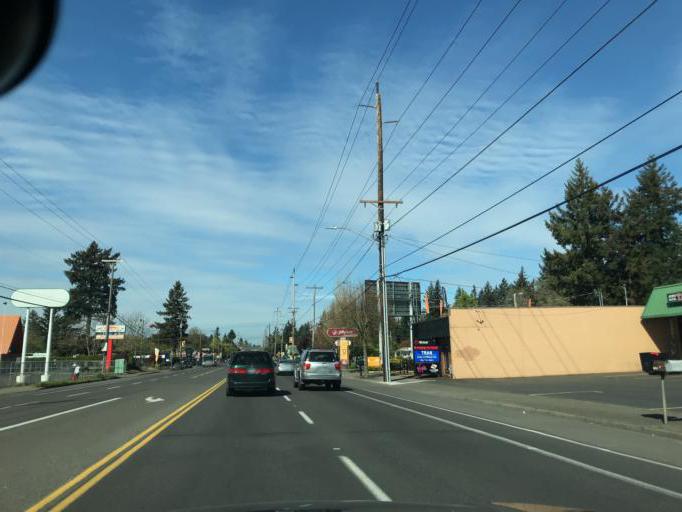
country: US
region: Oregon
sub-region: Multnomah County
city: Lents
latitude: 45.5042
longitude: -122.5139
